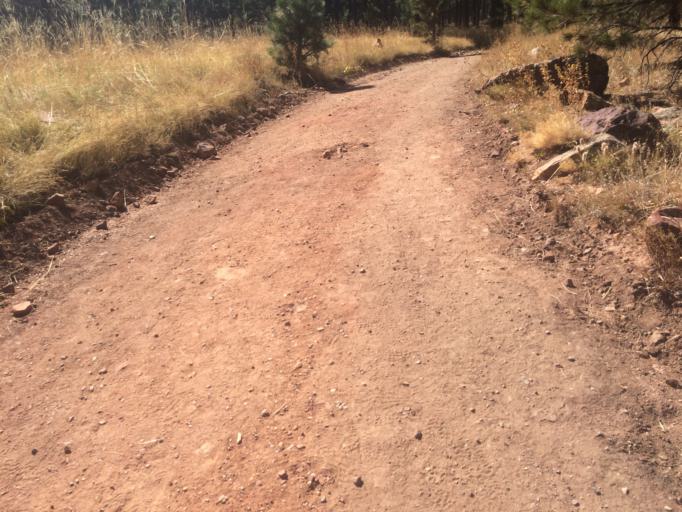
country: US
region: Colorado
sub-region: Boulder County
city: Boulder
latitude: 39.9653
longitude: -105.2739
